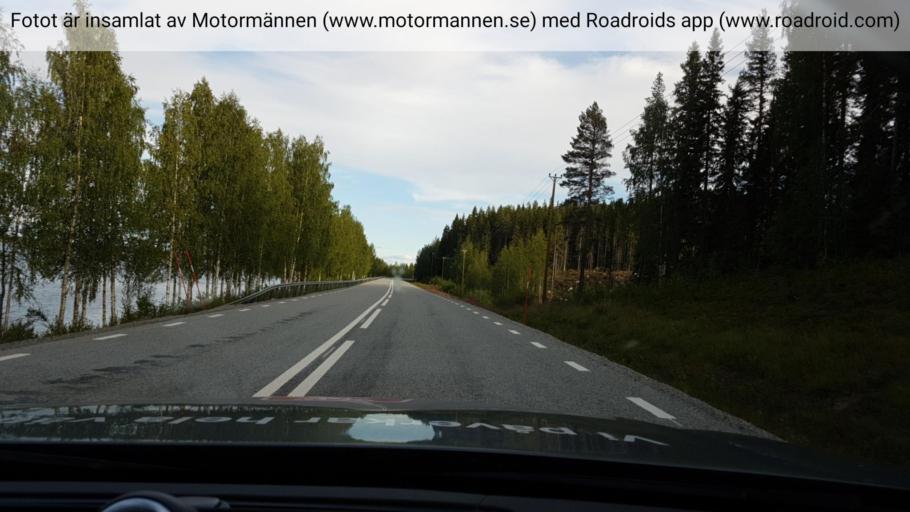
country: SE
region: Jaemtland
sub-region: Stroemsunds Kommun
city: Stroemsund
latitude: 64.1851
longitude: 15.6461
